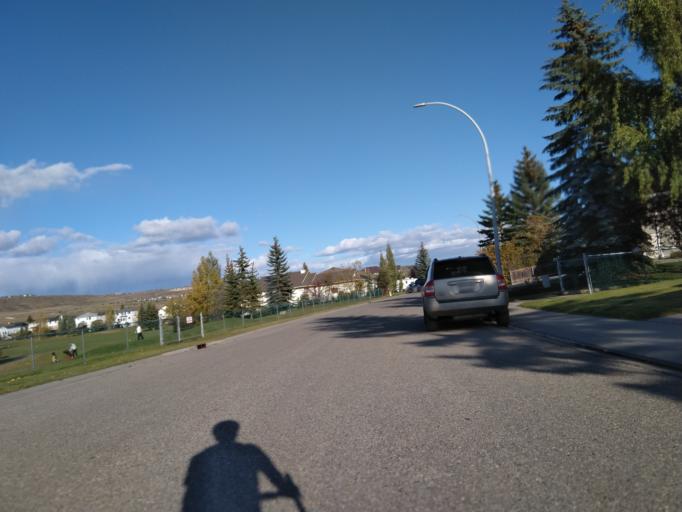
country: CA
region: Alberta
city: Cochrane
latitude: 51.1736
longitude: -114.4729
